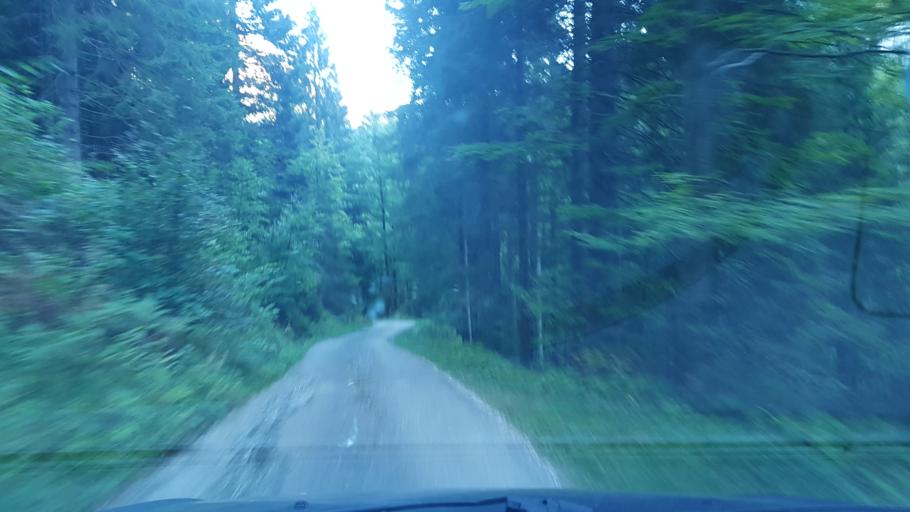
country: IT
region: Veneto
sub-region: Provincia di Belluno
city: Fusine
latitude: 46.3495
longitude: 12.0928
